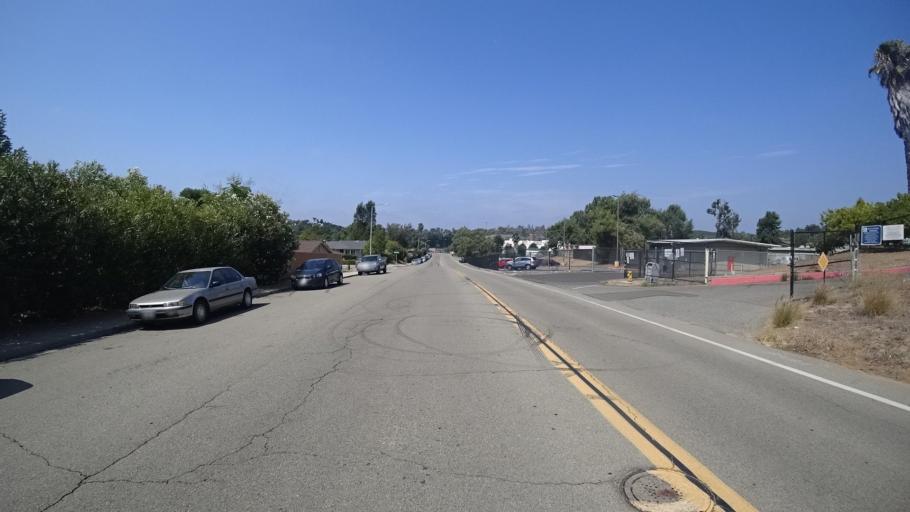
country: US
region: California
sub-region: San Diego County
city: Fallbrook
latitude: 33.3474
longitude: -117.2374
